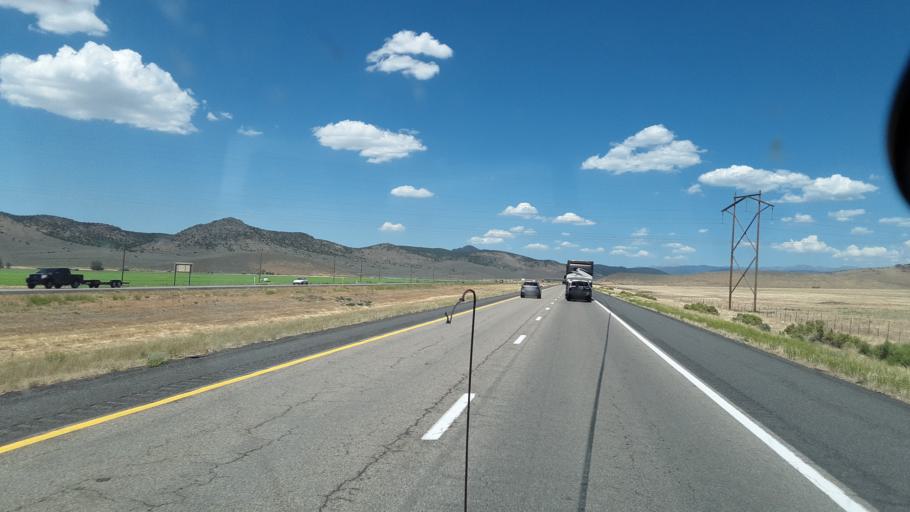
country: US
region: Utah
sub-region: Beaver County
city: Beaver
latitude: 38.0556
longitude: -112.6982
